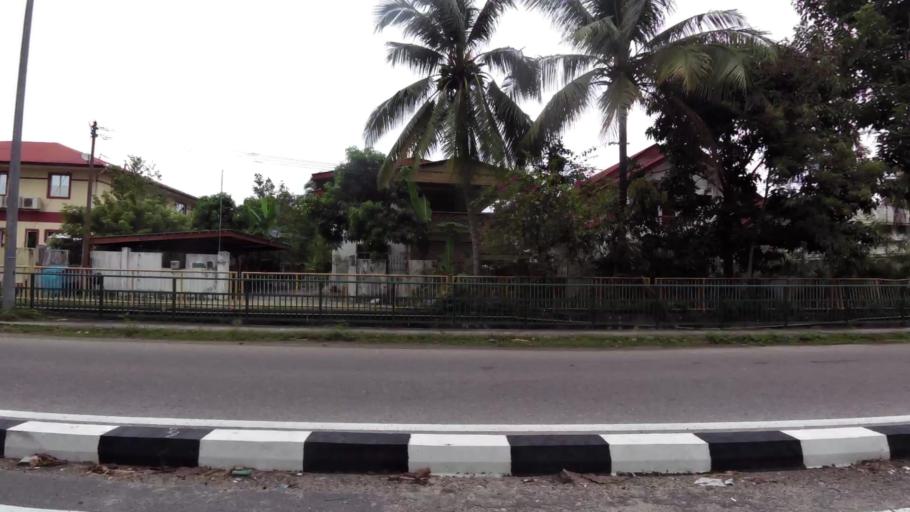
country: BN
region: Brunei and Muara
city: Bandar Seri Begawan
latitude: 4.8942
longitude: 114.9194
